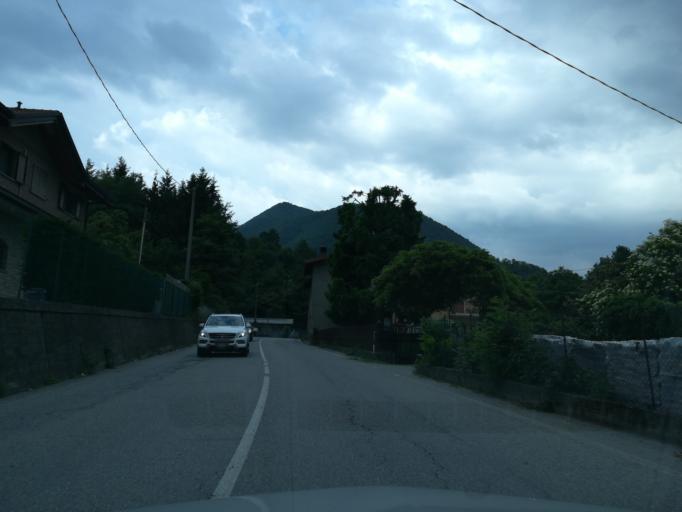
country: IT
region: Lombardy
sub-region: Provincia di Bergamo
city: Almenno San Salvatore
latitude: 45.7565
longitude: 9.5963
